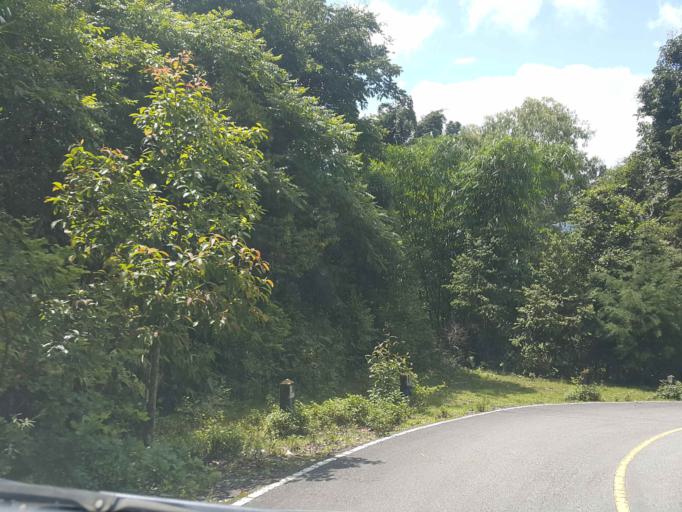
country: TH
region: Chiang Mai
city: Mae Chaem
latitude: 18.5151
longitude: 98.5294
